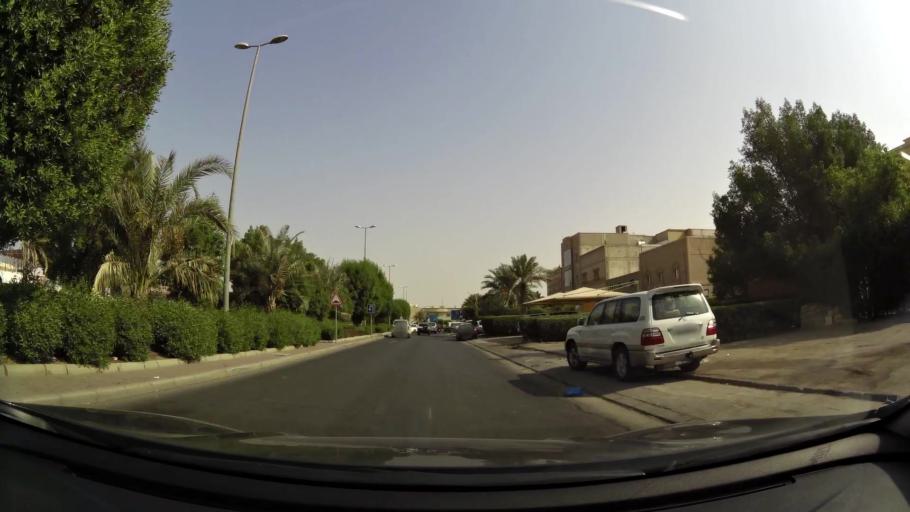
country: KW
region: Muhafazat al Jahra'
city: Al Jahra'
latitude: 29.3283
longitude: 47.6611
